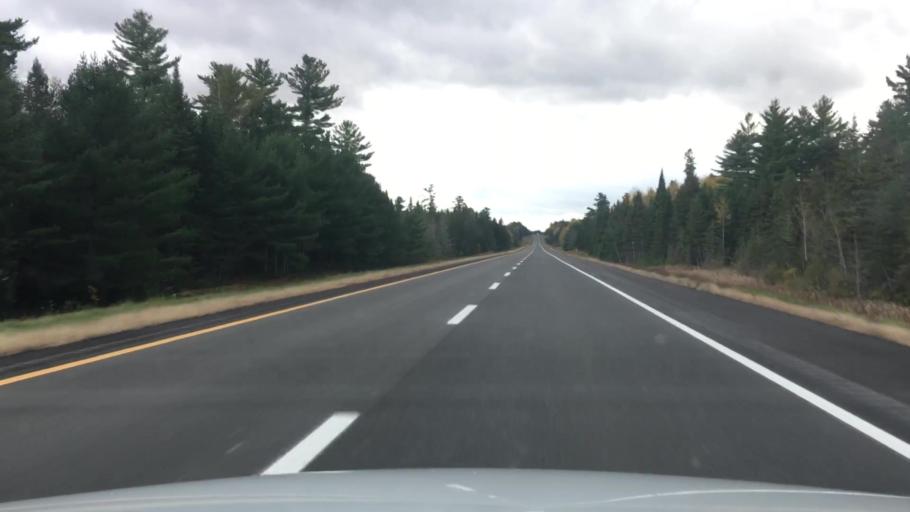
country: US
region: Maine
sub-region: Penobscot County
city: Patten
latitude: 46.0722
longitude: -68.2225
